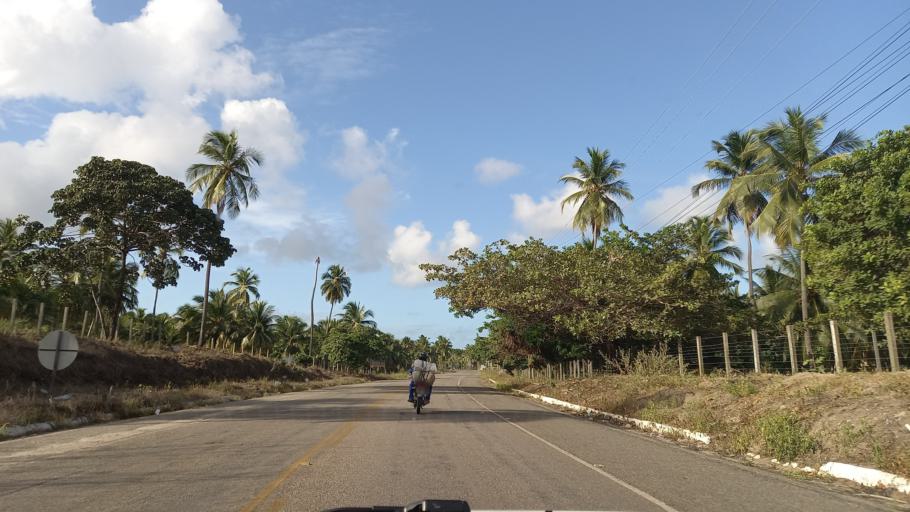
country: BR
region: Pernambuco
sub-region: Tamandare
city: Tamandare
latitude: -8.7100
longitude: -35.0895
